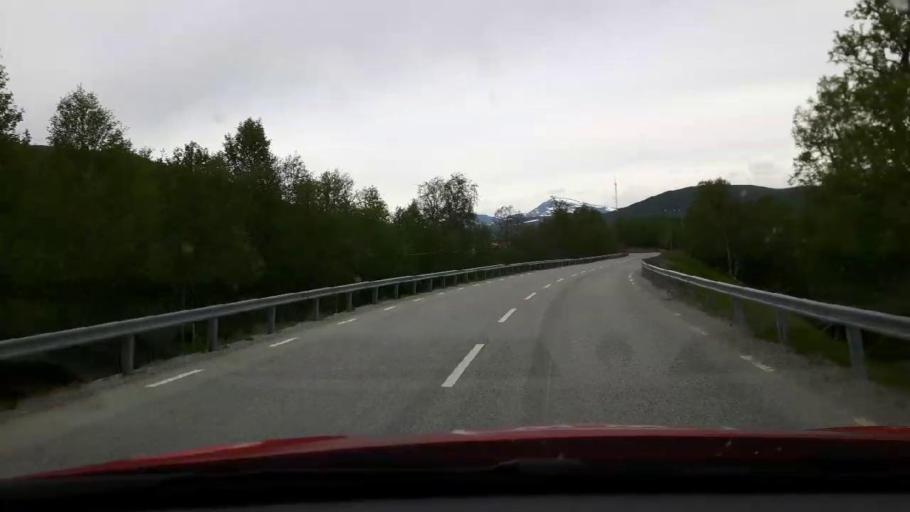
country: NO
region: Sor-Trondelag
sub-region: Tydal
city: Aas
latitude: 62.6985
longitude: 12.3957
